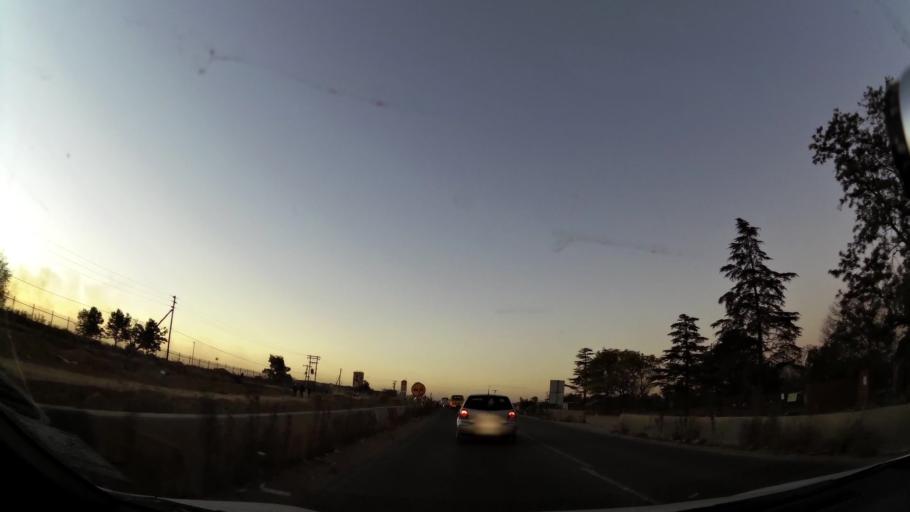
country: ZA
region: Gauteng
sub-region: City of Johannesburg Metropolitan Municipality
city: Diepsloot
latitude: -25.9445
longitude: 28.0197
